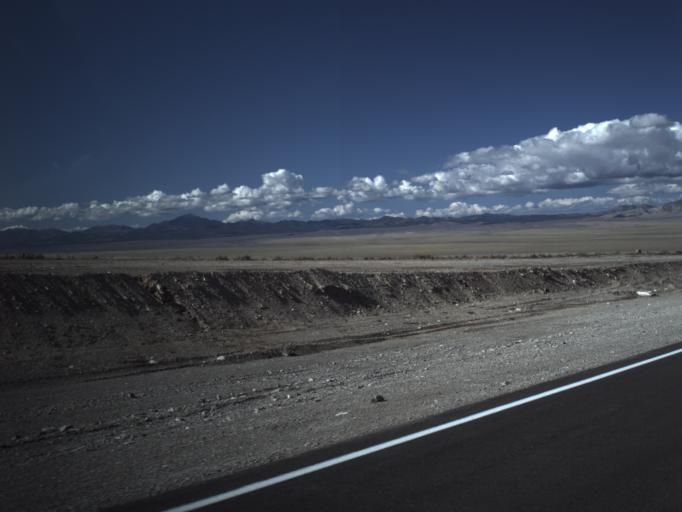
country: US
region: Utah
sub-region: Beaver County
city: Milford
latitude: 38.5058
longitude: -113.6050
